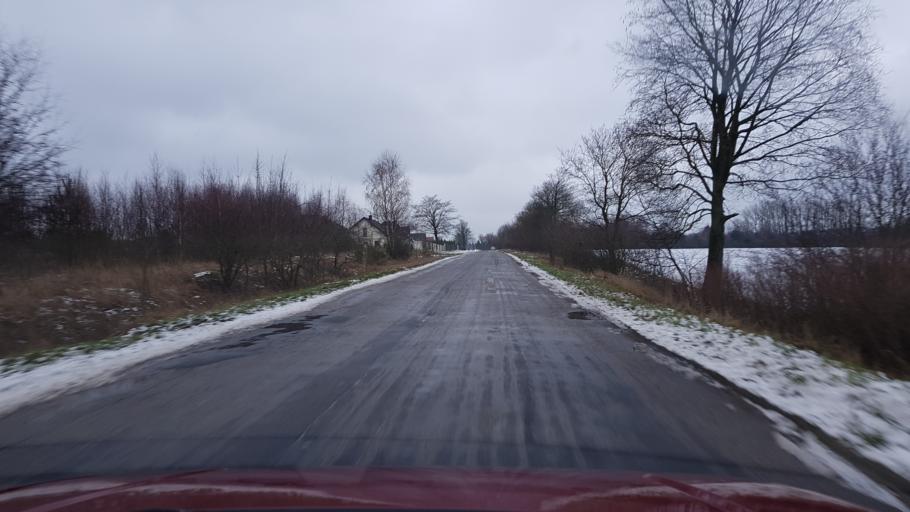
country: PL
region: West Pomeranian Voivodeship
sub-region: Powiat goleniowski
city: Nowogard
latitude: 53.6532
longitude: 15.1243
